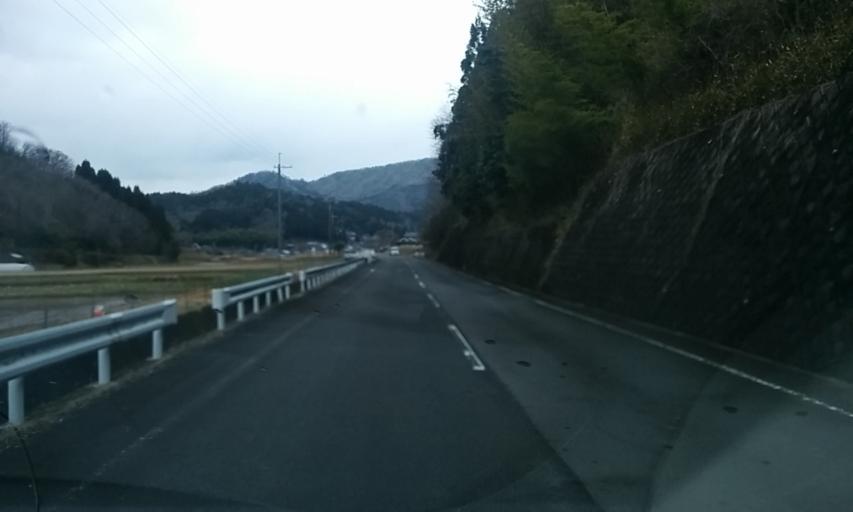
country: JP
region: Kyoto
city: Kameoka
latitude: 35.1221
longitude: 135.4179
